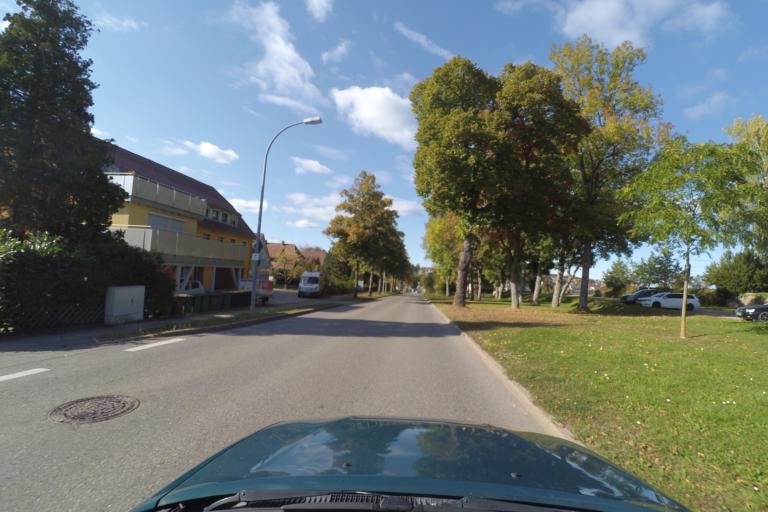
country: DE
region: Baden-Wuerttemberg
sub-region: Karlsruhe Region
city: Neubulach
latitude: 48.6641
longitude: 8.6900
